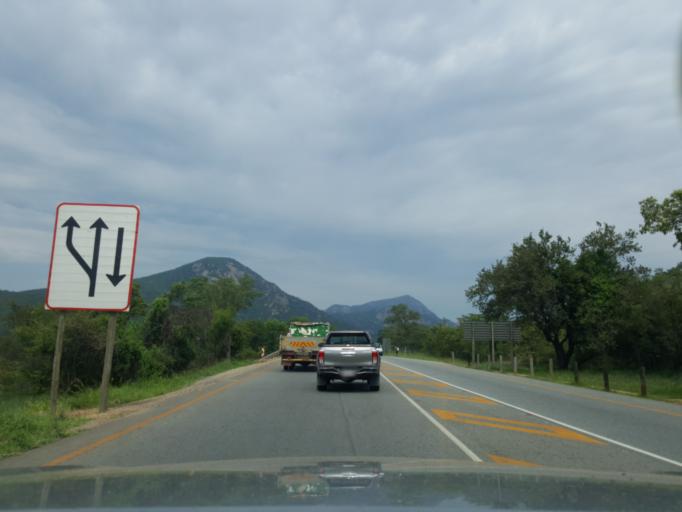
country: SZ
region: Hhohho
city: Ntfonjeni
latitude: -25.5368
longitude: 31.3004
